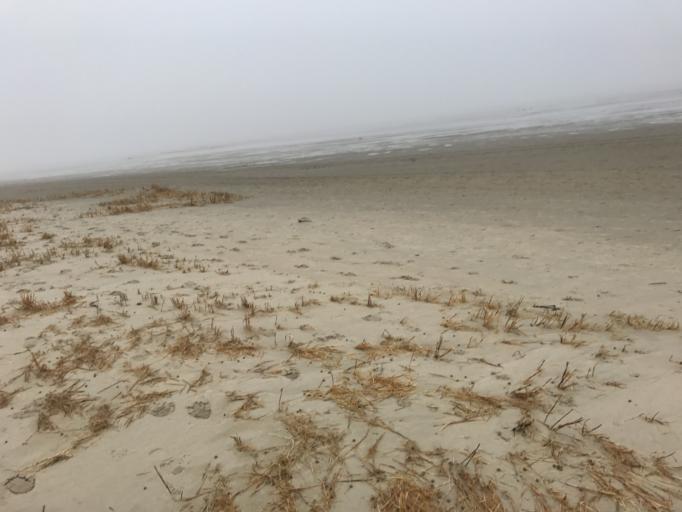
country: DE
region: Lower Saxony
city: Borkum
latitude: 53.6062
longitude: 6.6975
